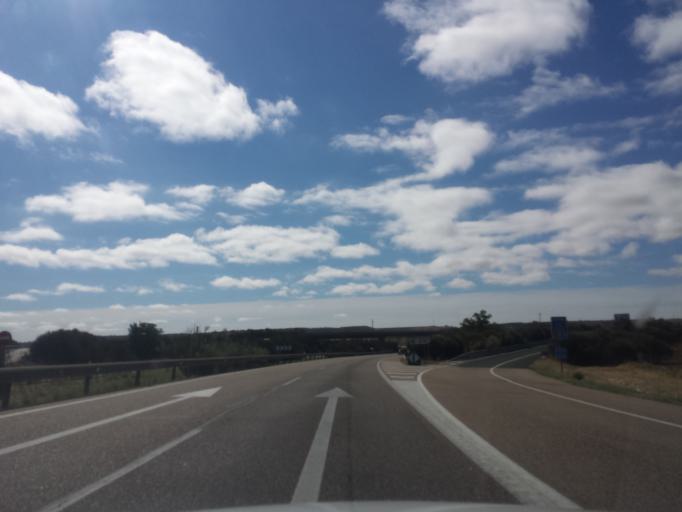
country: ES
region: Castille and Leon
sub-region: Provincia de Valladolid
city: Villardefrades
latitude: 41.7288
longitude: -5.2519
